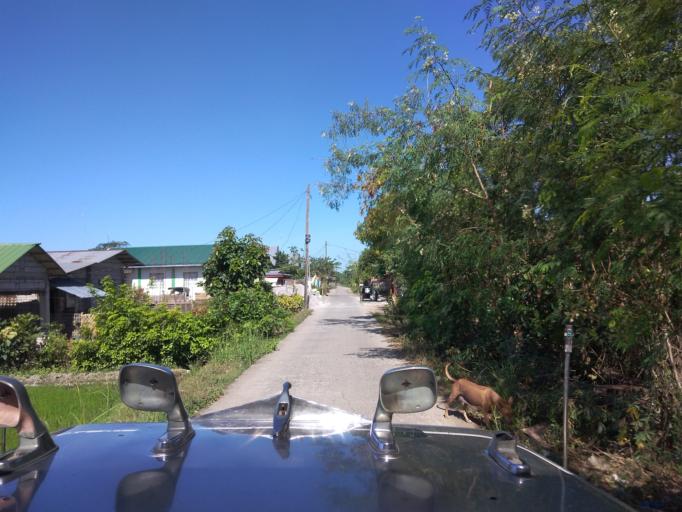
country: PH
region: Central Luzon
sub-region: Province of Pampanga
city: Salapungan
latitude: 15.1535
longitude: 120.9221
